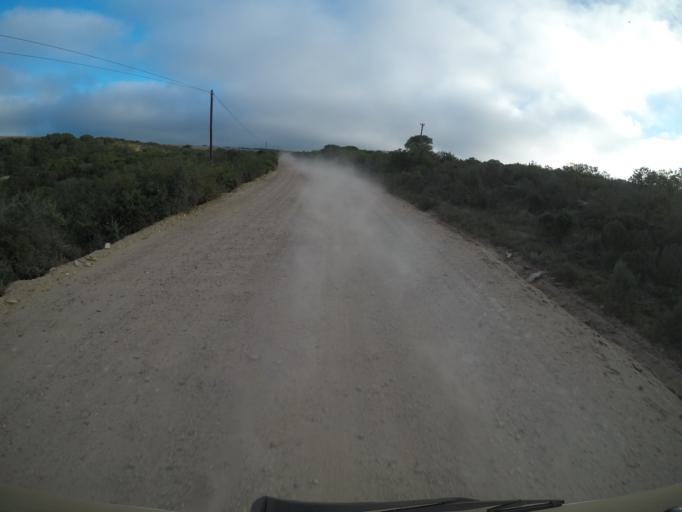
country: ZA
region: Western Cape
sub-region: Eden District Municipality
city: Mossel Bay
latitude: -34.1349
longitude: 22.0420
